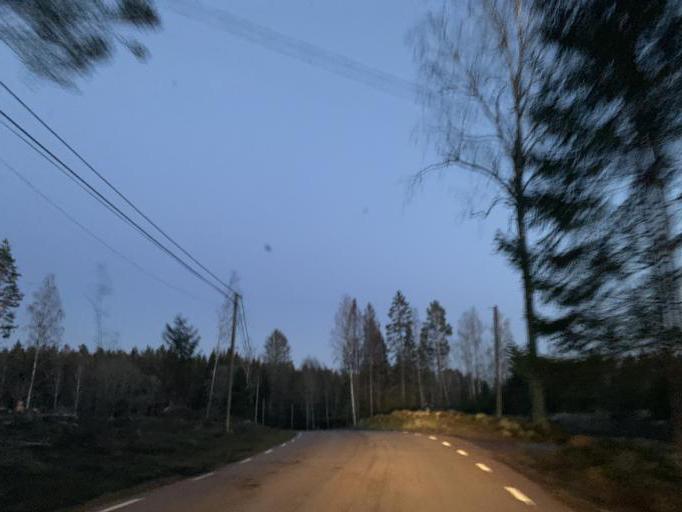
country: SE
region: OErebro
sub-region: Lindesbergs Kommun
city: Fellingsbro
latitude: 59.3743
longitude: 15.6351
